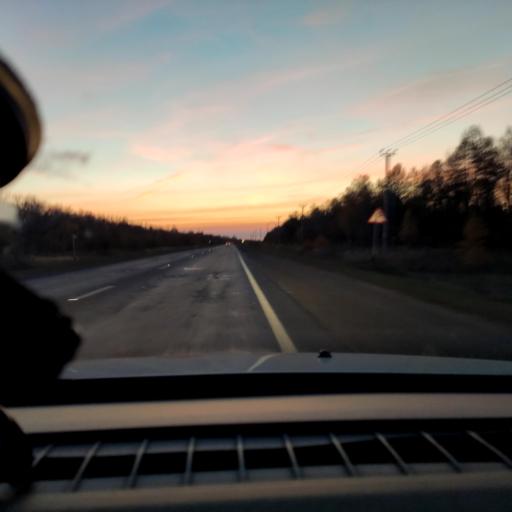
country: RU
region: Samara
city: Chapayevsk
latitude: 52.9960
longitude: 49.7982
